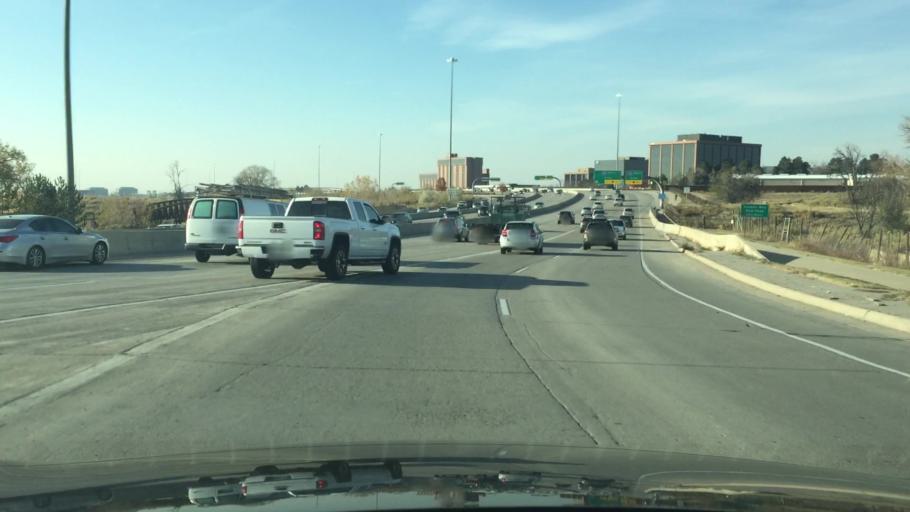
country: US
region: Colorado
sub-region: Arapahoe County
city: Dove Valley
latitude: 39.6534
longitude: -104.8319
